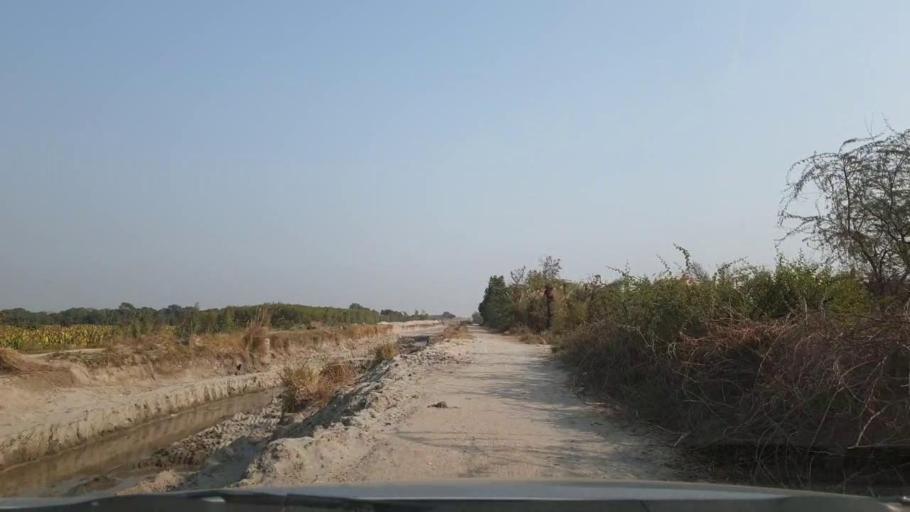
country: PK
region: Sindh
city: Tando Adam
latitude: 25.6495
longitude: 68.5932
